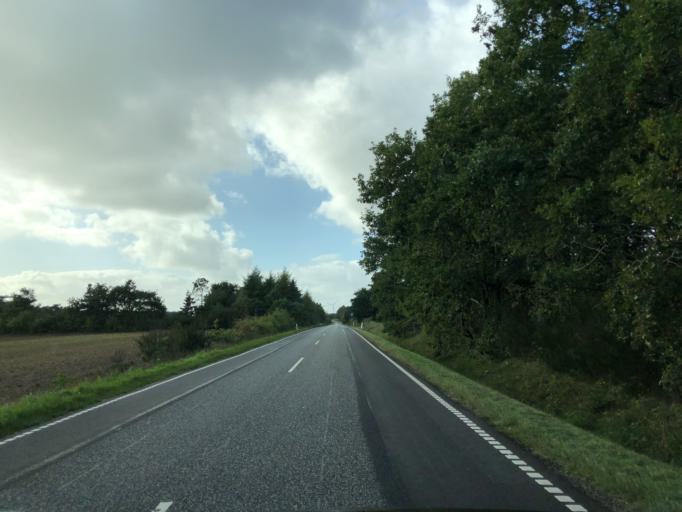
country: DK
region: Central Jutland
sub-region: Holstebro Kommune
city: Holstebro
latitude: 56.3718
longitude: 8.5289
